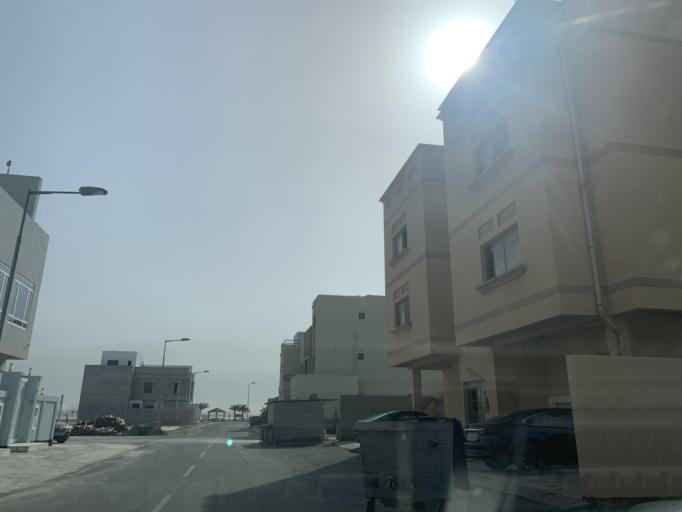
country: BH
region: Northern
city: Madinat `Isa
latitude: 26.1876
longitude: 50.5656
